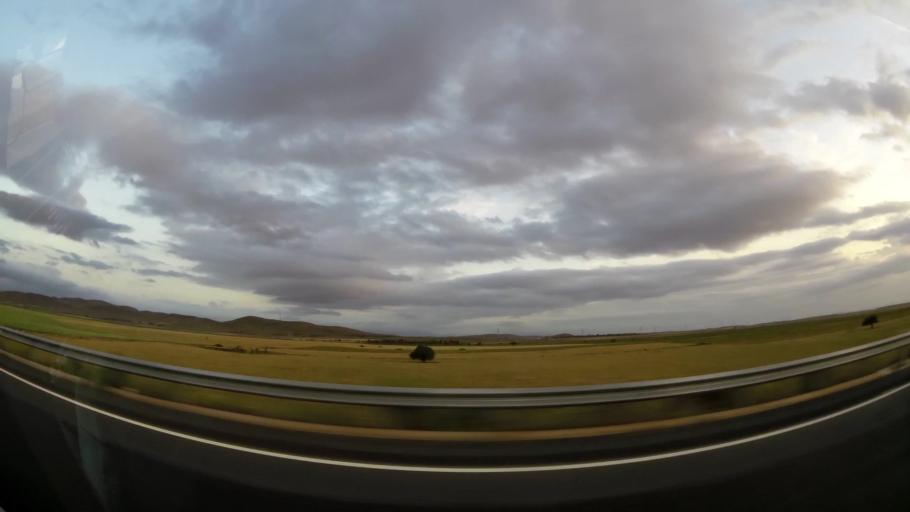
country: MA
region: Oriental
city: El Aioun
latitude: 34.5976
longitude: -2.7222
